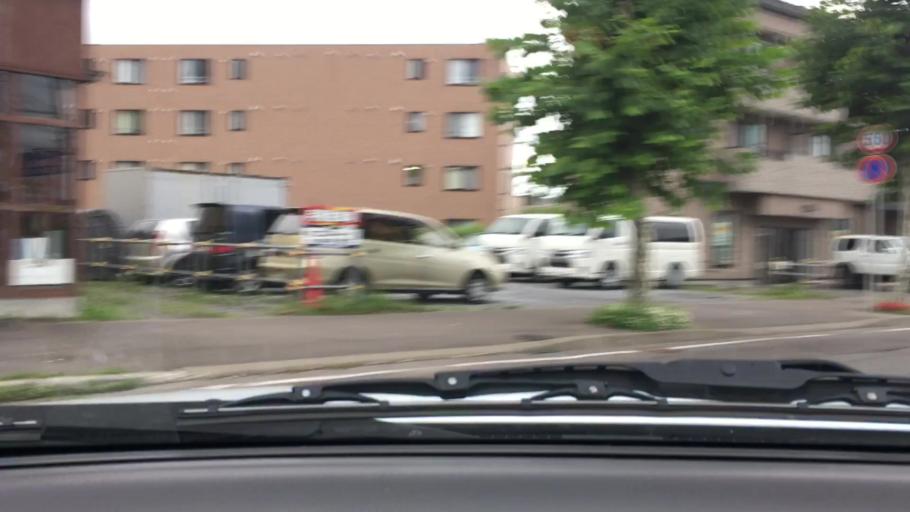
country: JP
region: Hokkaido
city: Hakodate
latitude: 41.8007
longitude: 140.7304
